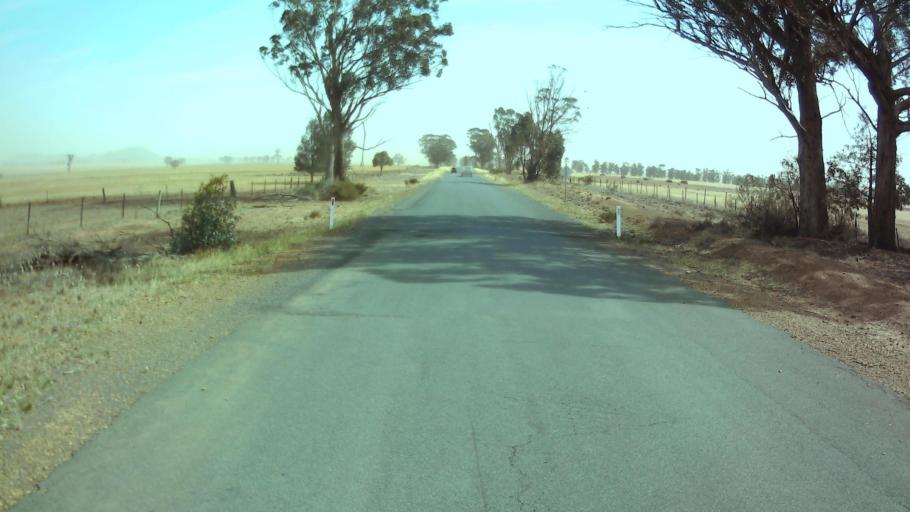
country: AU
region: New South Wales
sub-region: Weddin
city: Grenfell
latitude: -33.7728
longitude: 147.9864
